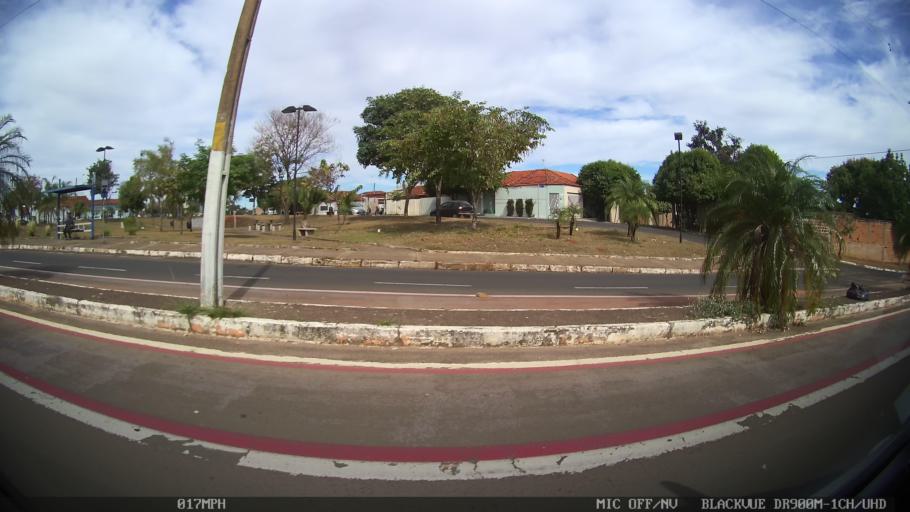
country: BR
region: Sao Paulo
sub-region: Catanduva
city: Catanduva
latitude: -21.1444
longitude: -48.9465
